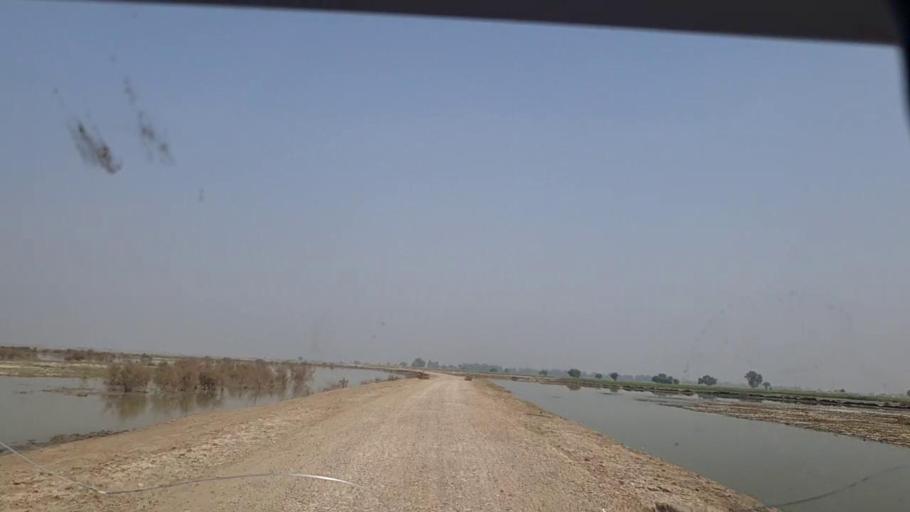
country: PK
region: Sindh
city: Shikarpur
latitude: 28.0406
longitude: 68.6481
